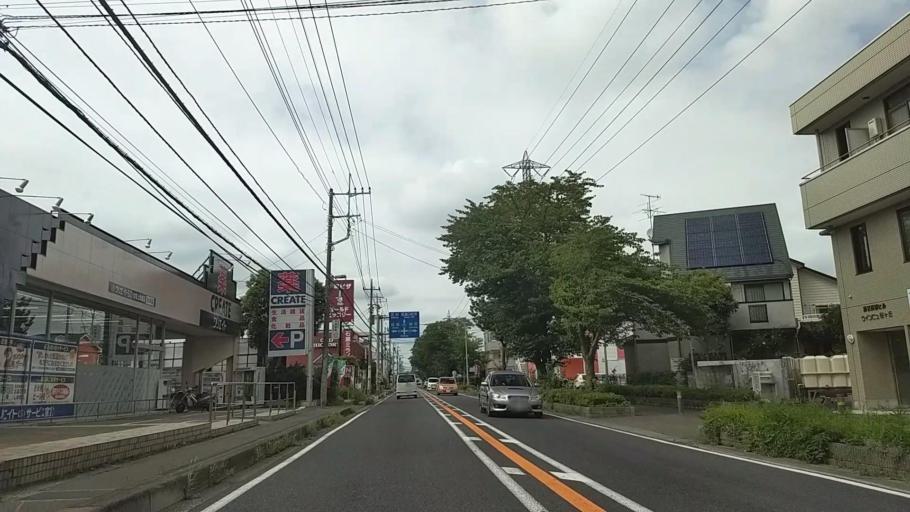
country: JP
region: Kanagawa
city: Minami-rinkan
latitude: 35.4458
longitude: 139.4674
